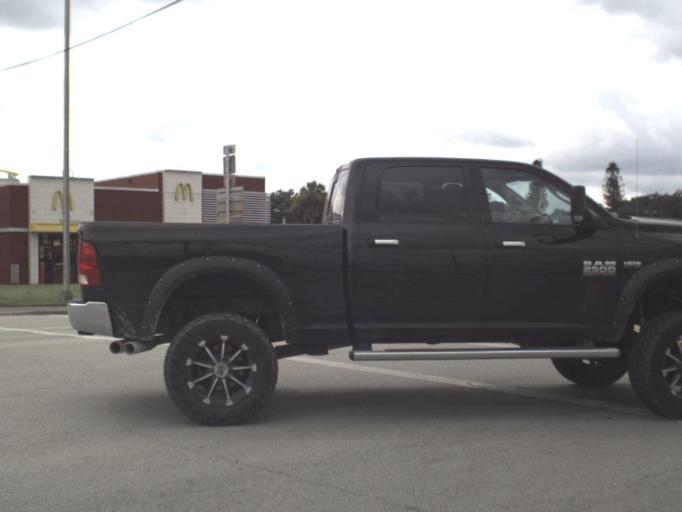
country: US
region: Florida
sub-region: Hendry County
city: LaBelle
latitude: 26.7619
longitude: -81.4385
